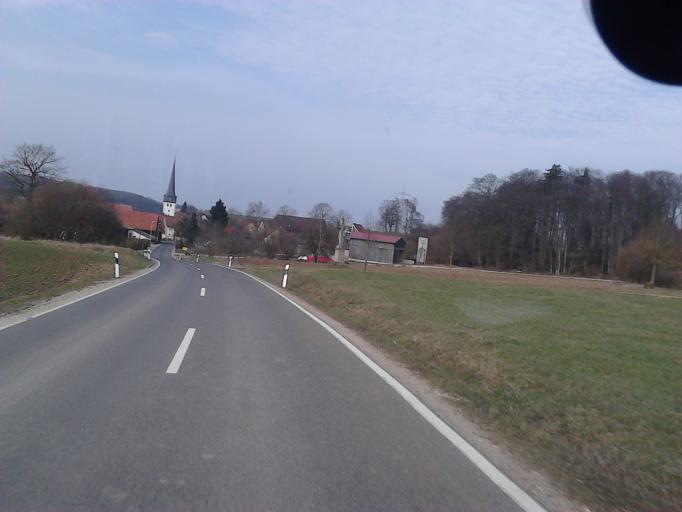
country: DE
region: Bavaria
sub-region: Upper Franconia
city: Wattendorf
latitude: 50.0293
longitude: 11.1242
